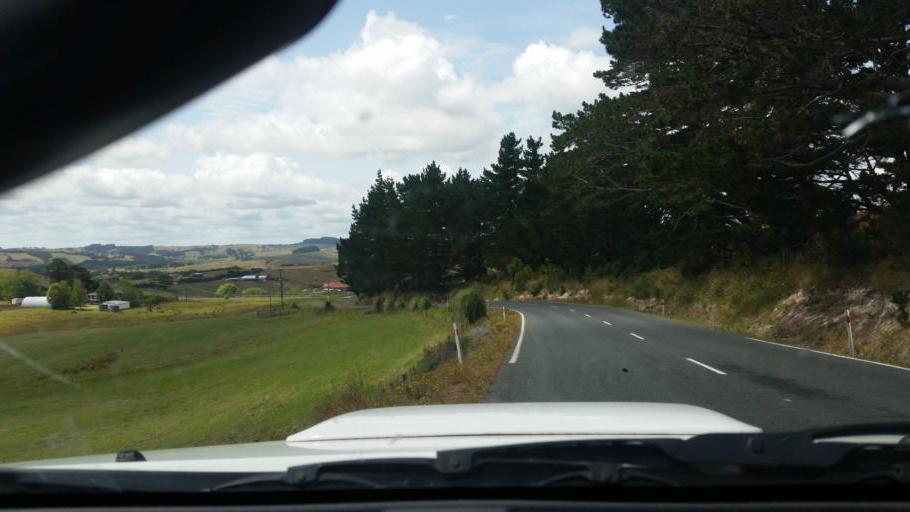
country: NZ
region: Auckland
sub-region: Auckland
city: Wellsford
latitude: -36.1422
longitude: 174.4869
